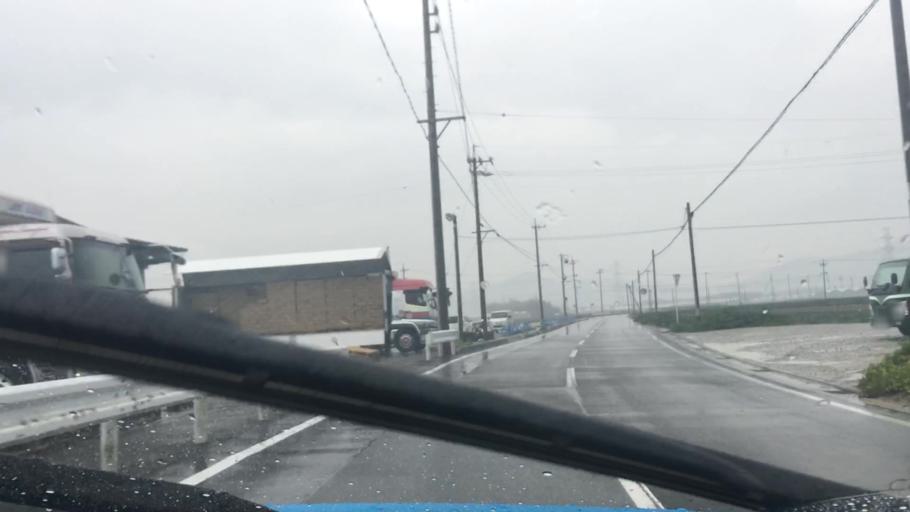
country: JP
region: Aichi
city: Tahara
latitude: 34.6480
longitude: 137.2946
